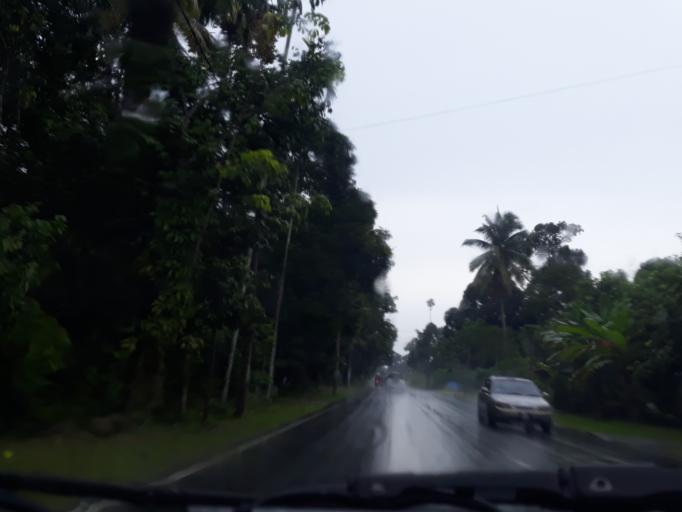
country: MY
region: Kedah
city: Kulim
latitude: 5.3591
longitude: 100.5822
